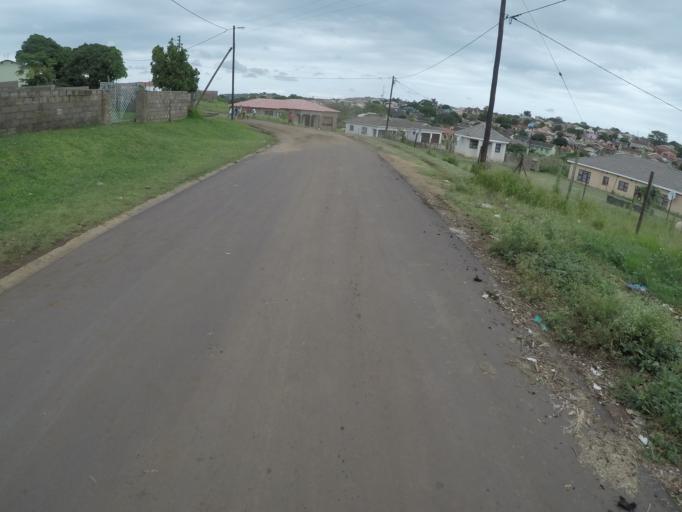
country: ZA
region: KwaZulu-Natal
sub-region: uThungulu District Municipality
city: Empangeni
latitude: -28.7742
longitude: 31.8532
